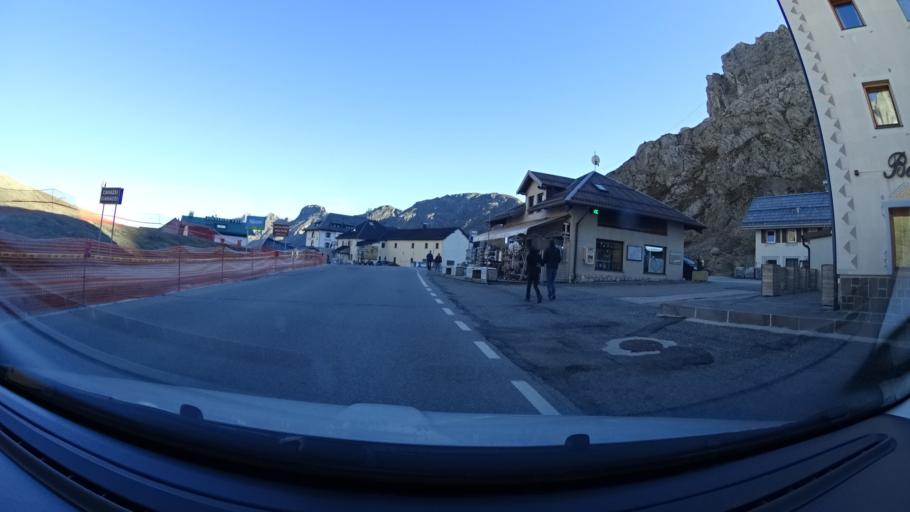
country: IT
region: Trentino-Alto Adige
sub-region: Provincia di Trento
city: Canazei
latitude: 46.4879
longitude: 11.8116
